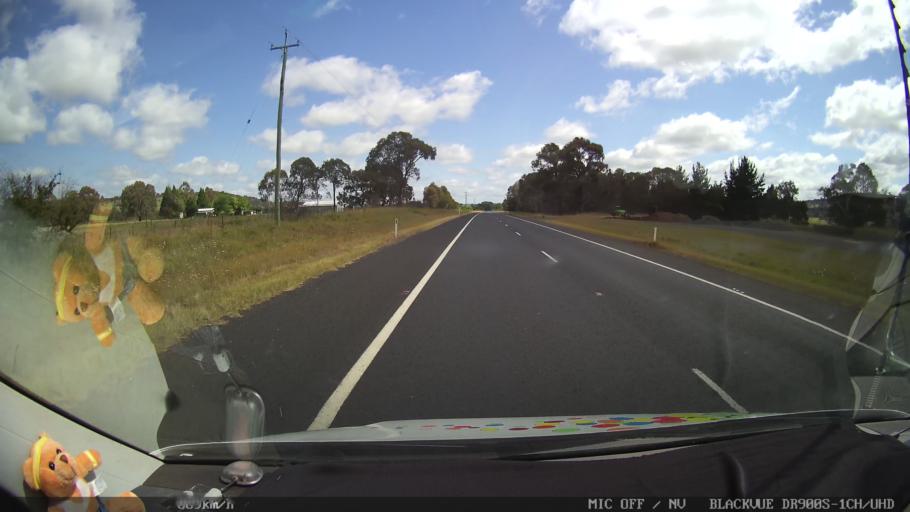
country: AU
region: New South Wales
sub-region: Glen Innes Severn
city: Glen Innes
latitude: -29.8707
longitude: 151.7357
